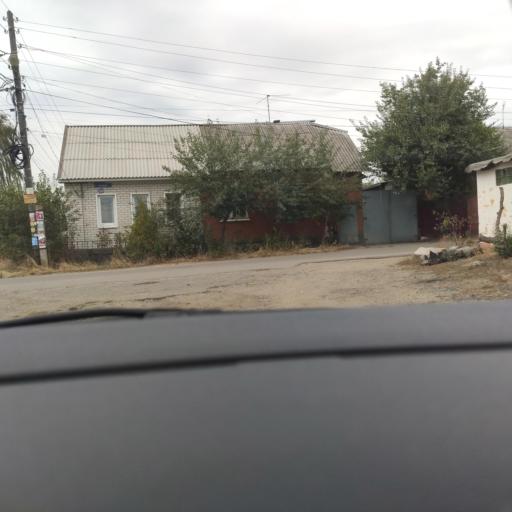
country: RU
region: Voronezj
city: Voronezh
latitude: 51.6356
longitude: 39.1606
